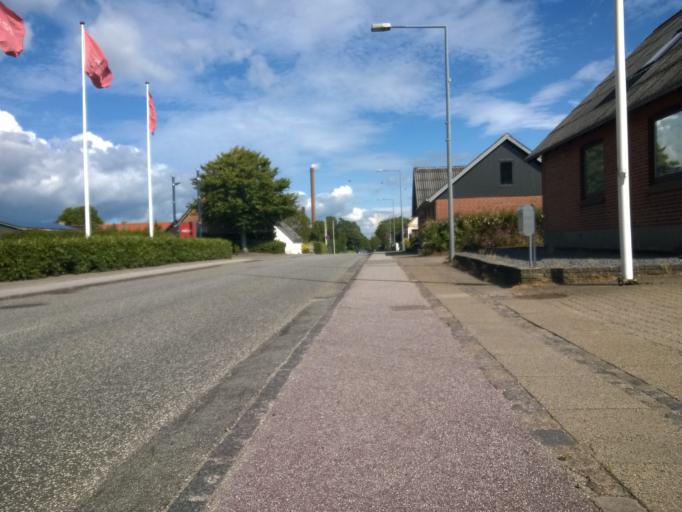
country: DK
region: Central Jutland
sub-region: Holstebro Kommune
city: Vinderup
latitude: 56.4782
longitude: 8.7865
